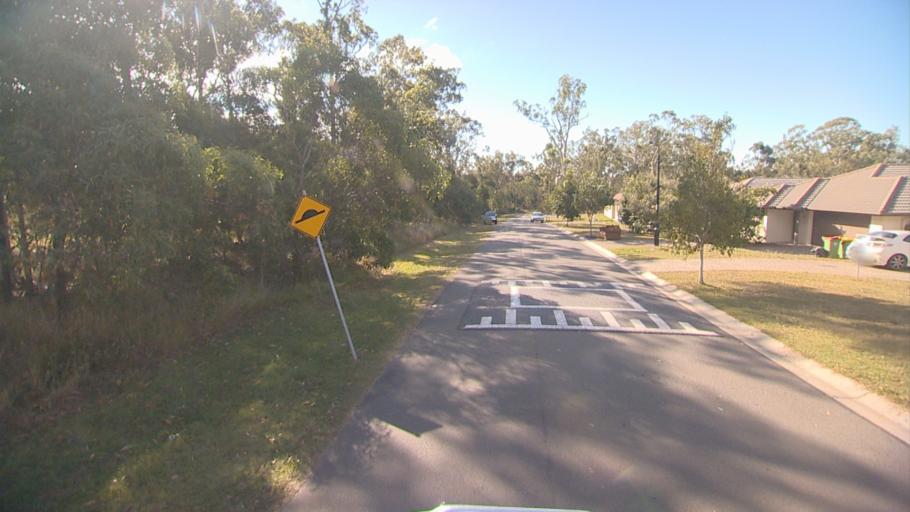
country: AU
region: Queensland
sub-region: Logan
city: Logan Reserve
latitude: -27.6936
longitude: 153.0951
